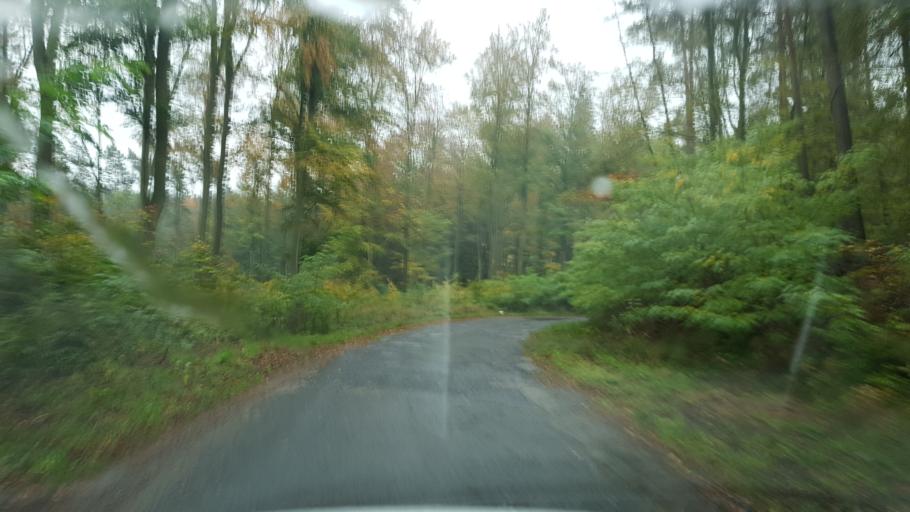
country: PL
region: West Pomeranian Voivodeship
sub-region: Powiat mysliborski
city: Barlinek
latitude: 53.0197
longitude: 15.2225
